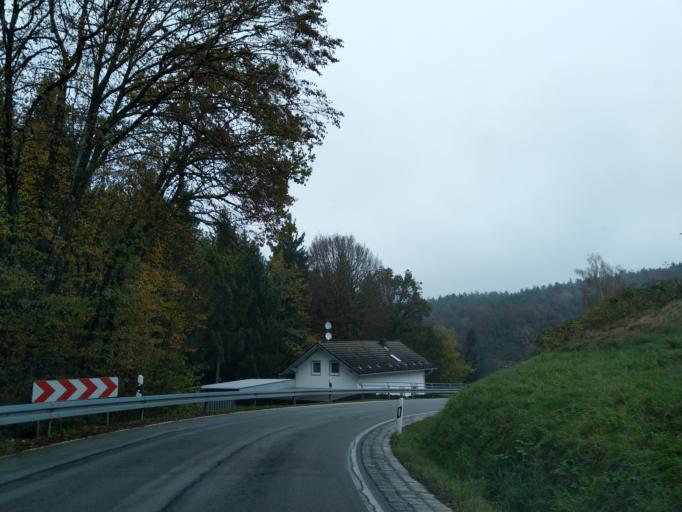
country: DE
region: Bavaria
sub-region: Lower Bavaria
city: Auerbach
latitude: 48.7968
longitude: 13.0982
